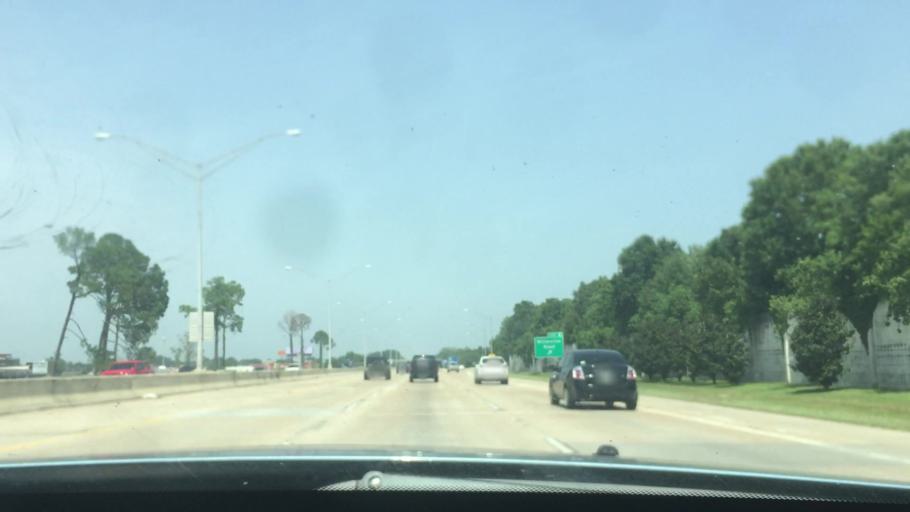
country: US
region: Louisiana
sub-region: East Baton Rouge Parish
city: Shenandoah
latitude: 30.4361
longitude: -91.0323
